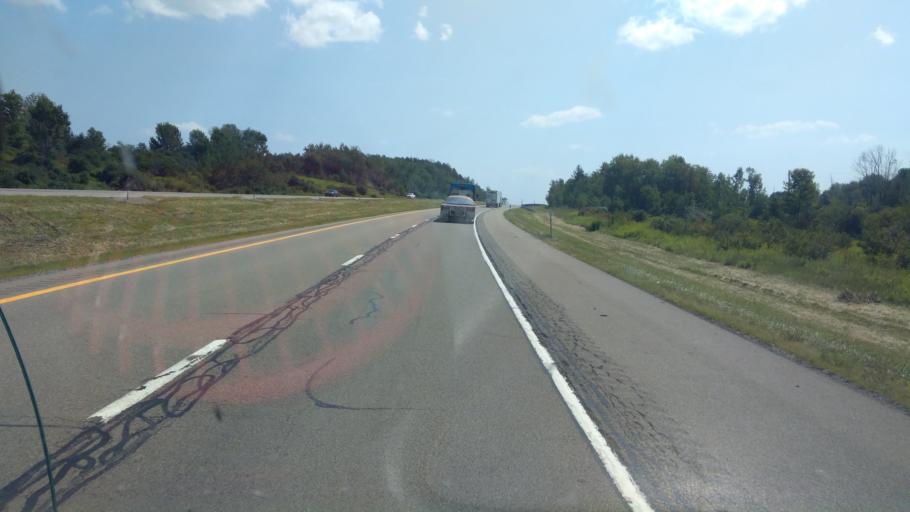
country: US
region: New York
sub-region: Steuben County
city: Canisteo
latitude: 42.3774
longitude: -77.5279
